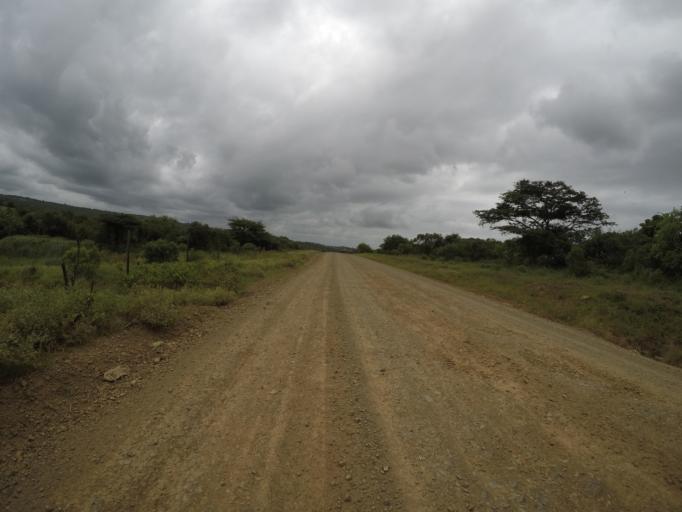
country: ZA
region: KwaZulu-Natal
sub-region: uThungulu District Municipality
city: Empangeni
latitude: -28.6009
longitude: 31.8276
